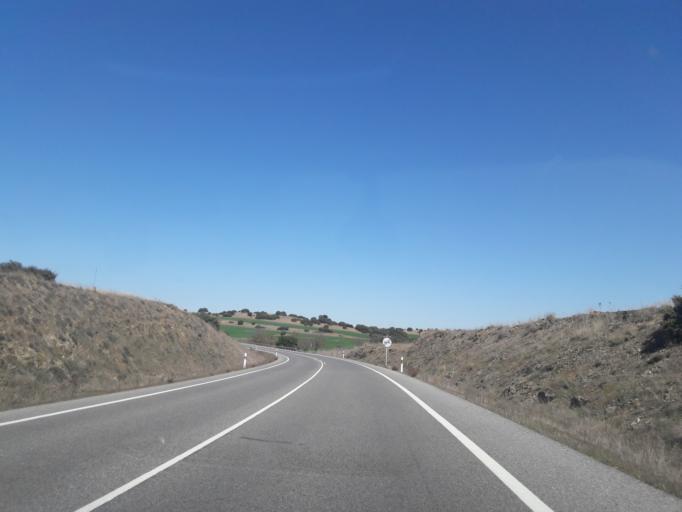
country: ES
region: Castille and Leon
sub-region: Provincia de Salamanca
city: Arapiles
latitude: 40.8775
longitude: -5.6590
